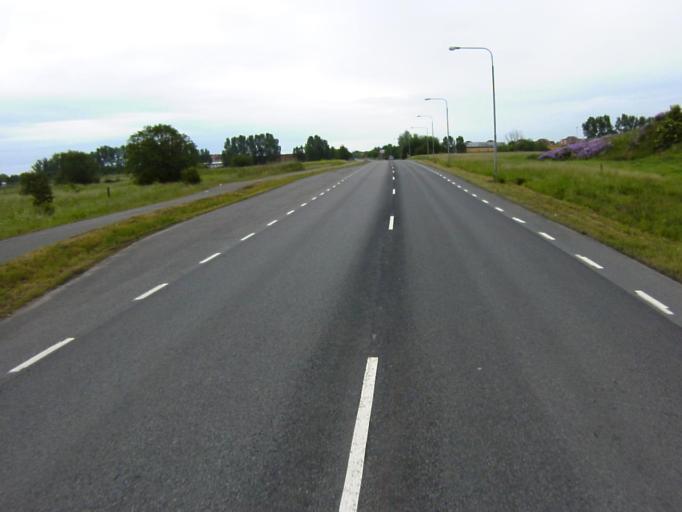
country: SE
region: Skane
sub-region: Kristianstads Kommun
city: Kristianstad
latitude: 56.0275
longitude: 14.1395
